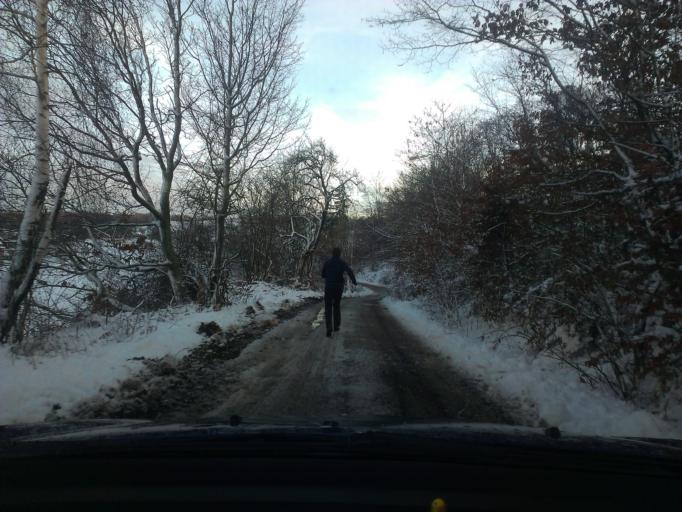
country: SK
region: Trnavsky
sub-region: Okres Trnava
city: Piestany
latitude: 48.6340
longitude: 17.9676
